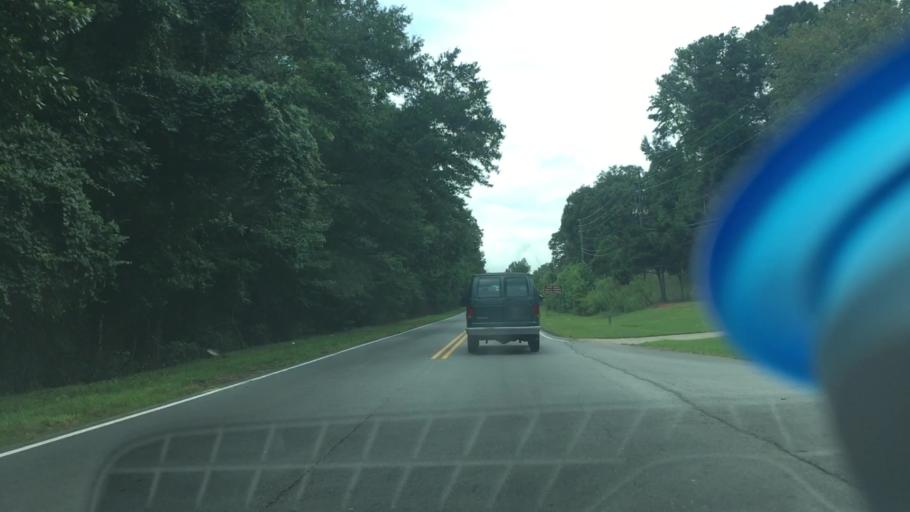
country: US
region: Georgia
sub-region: Rockdale County
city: Conyers
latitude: 33.6894
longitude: -84.0131
